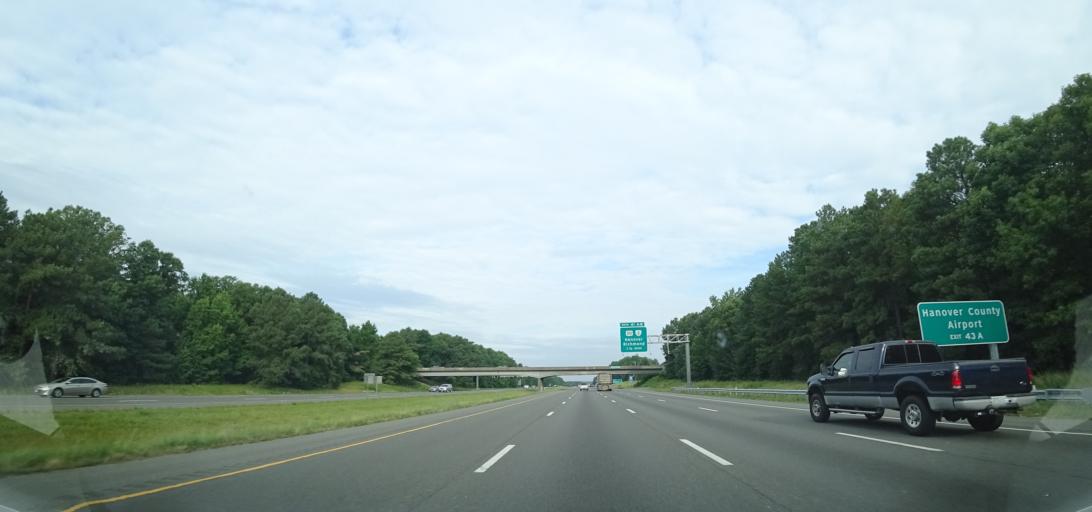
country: US
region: Virginia
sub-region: Hanover County
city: Mechanicsville
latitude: 37.6335
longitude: -77.3855
